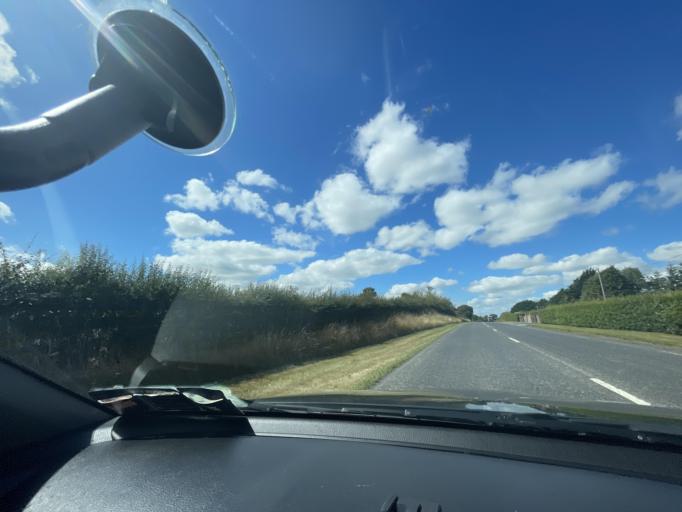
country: IE
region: Leinster
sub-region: An Mhi
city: Newtown Trim
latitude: 53.5299
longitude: -6.6880
